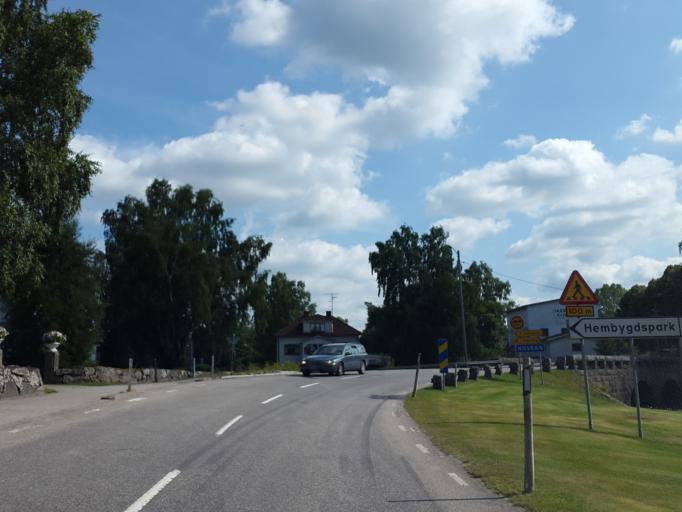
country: SE
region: Vaestra Goetaland
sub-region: Herrljunga Kommun
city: Herrljunga
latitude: 58.0545
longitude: 13.0927
